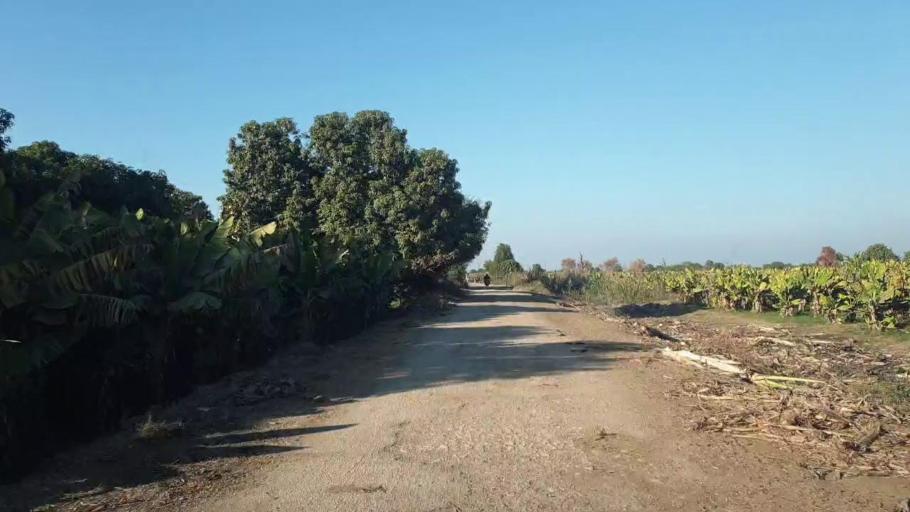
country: PK
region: Sindh
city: Shahdadpur
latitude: 25.9227
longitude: 68.5992
